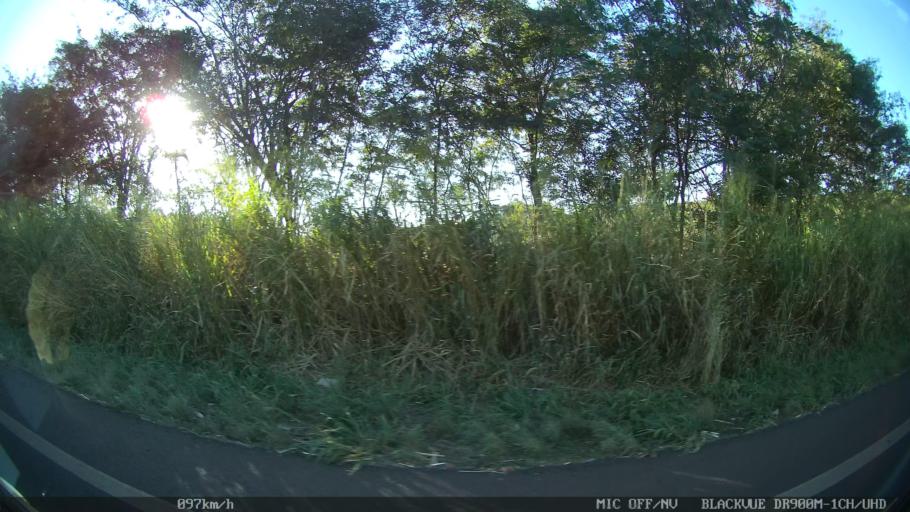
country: BR
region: Sao Paulo
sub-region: Guapiacu
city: Guapiacu
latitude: -20.7697
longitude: -49.2123
